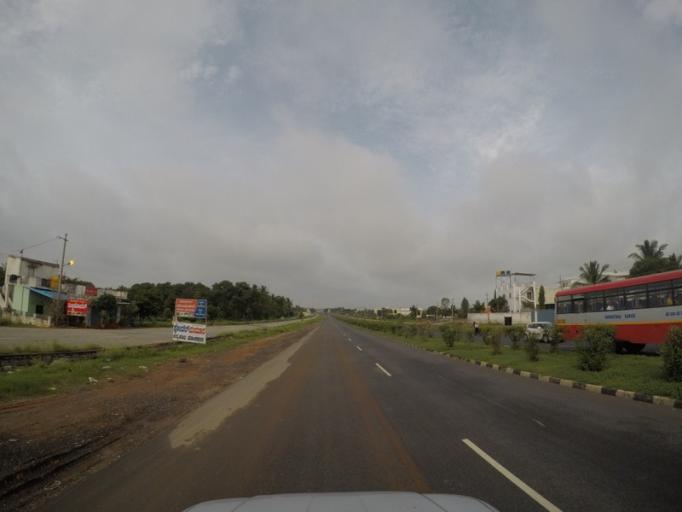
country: IN
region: Karnataka
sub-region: Bangalore Rural
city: Nelamangala
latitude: 13.0653
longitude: 77.3538
